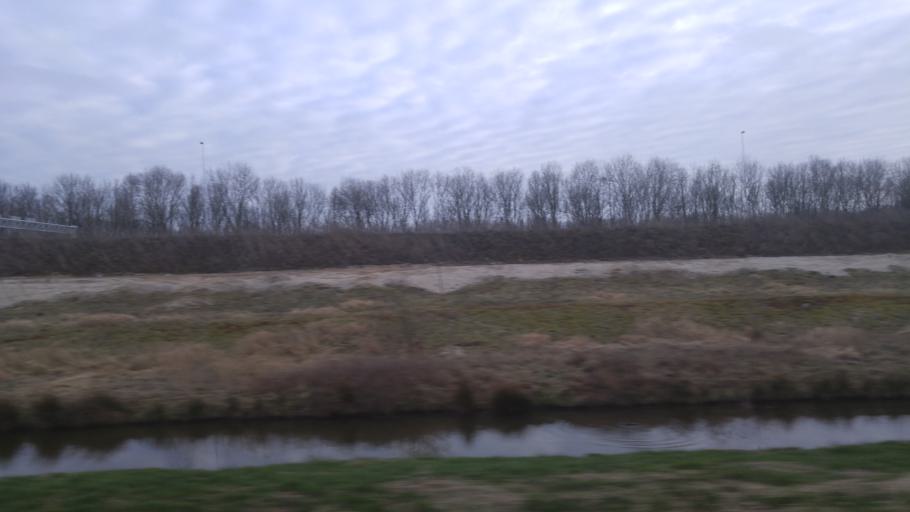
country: NL
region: Utrecht
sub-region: Gemeente Woerden
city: Woerden
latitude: 52.0707
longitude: 4.8663
